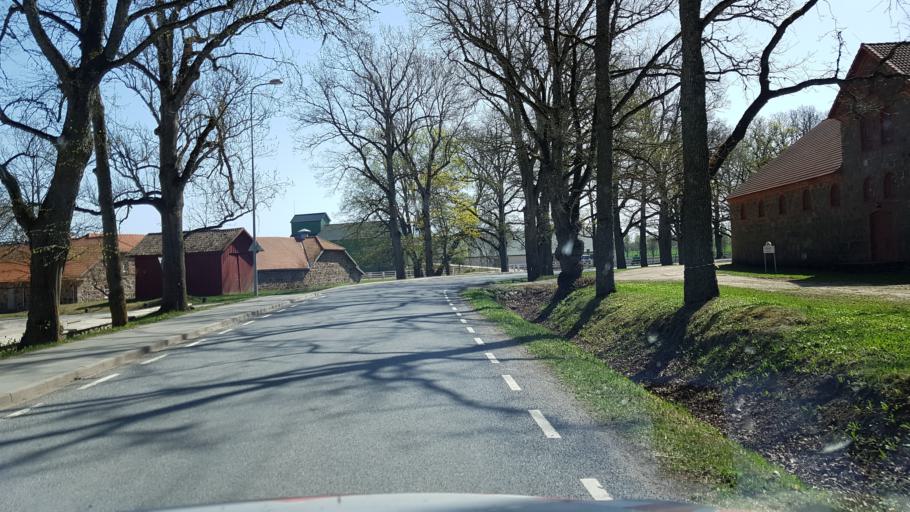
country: EE
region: Viljandimaa
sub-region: Vohma linn
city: Vohma
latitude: 58.5528
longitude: 25.5638
